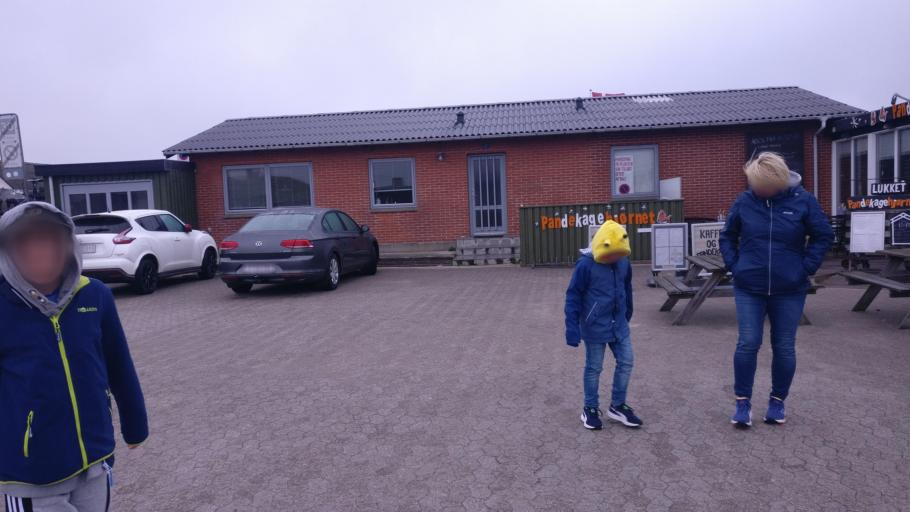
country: DK
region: North Denmark
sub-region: Thisted Kommune
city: Hurup
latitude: 56.9581
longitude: 8.3676
